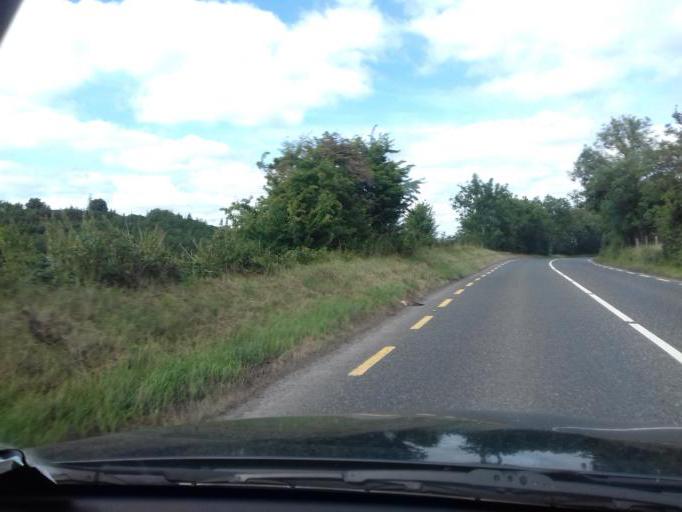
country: IE
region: Leinster
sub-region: Wicklow
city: Valleymount
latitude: 53.0522
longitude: -6.6289
